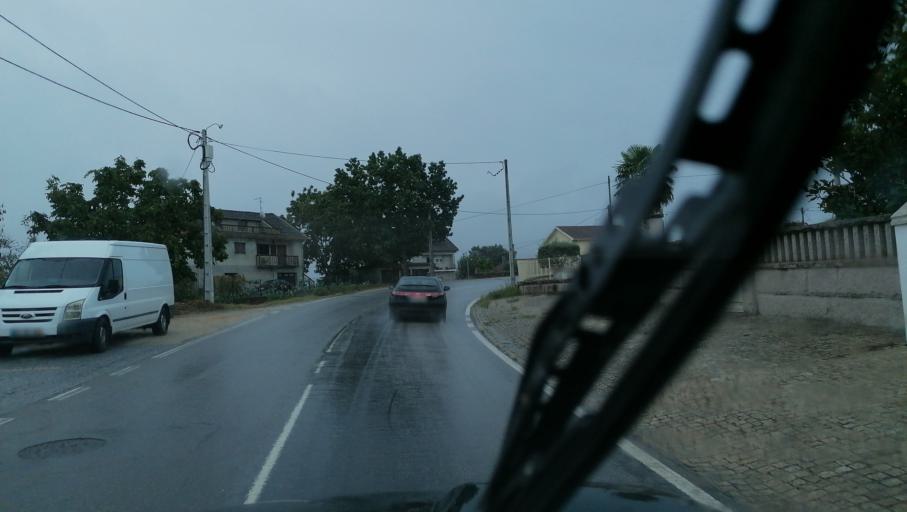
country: PT
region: Braga
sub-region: Cabeceiras de Basto
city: Cabeceiras de Basto
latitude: 41.4973
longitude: -7.9086
